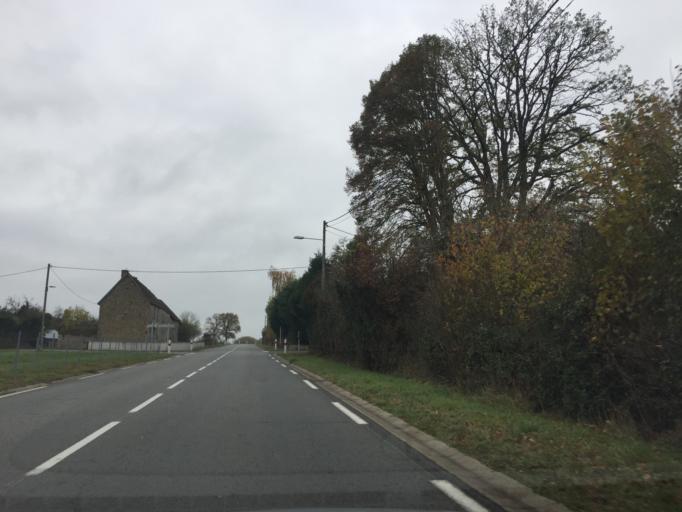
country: FR
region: Limousin
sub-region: Departement de la Creuse
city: Gouzon
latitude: 46.1389
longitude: 2.1981
